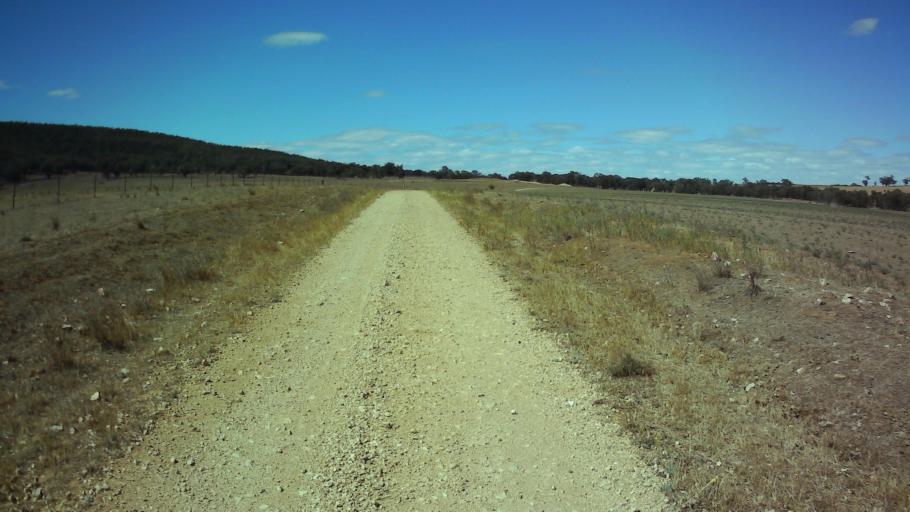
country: AU
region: New South Wales
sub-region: Weddin
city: Grenfell
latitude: -34.0368
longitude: 148.4336
